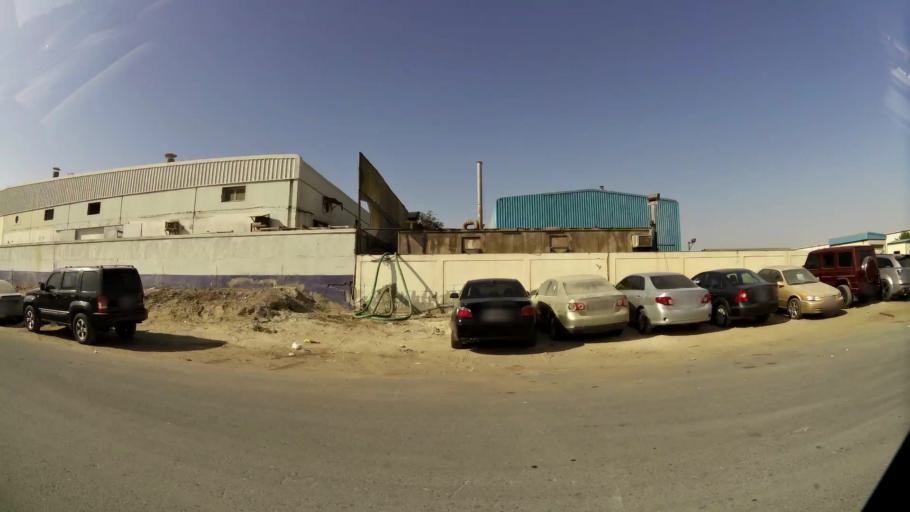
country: AE
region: Dubai
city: Dubai
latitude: 25.1196
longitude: 55.2096
